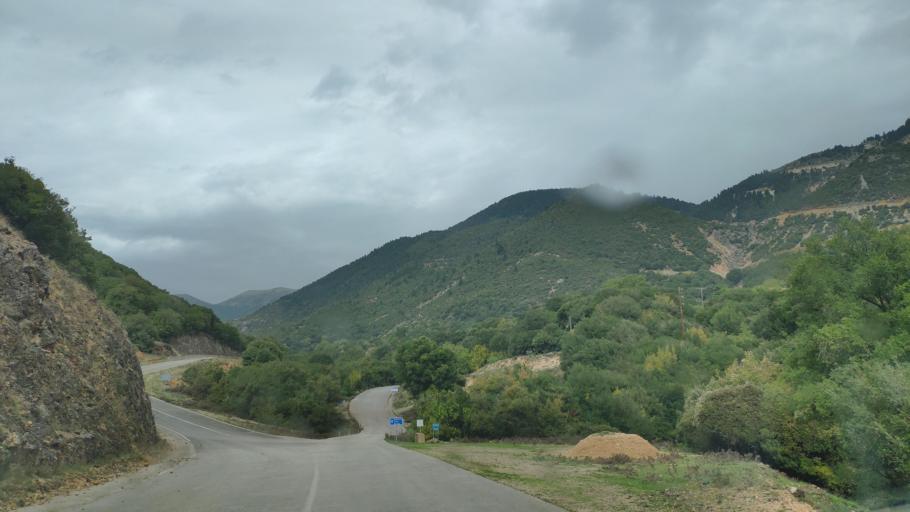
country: GR
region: Epirus
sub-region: Nomos Thesprotias
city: Paramythia
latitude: 39.4300
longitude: 20.6250
